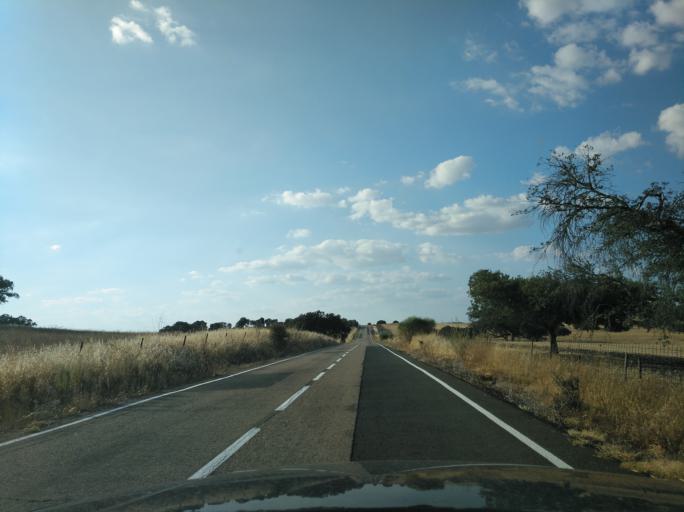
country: PT
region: Portalegre
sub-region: Campo Maior
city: Campo Maior
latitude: 39.1182
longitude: -7.0560
